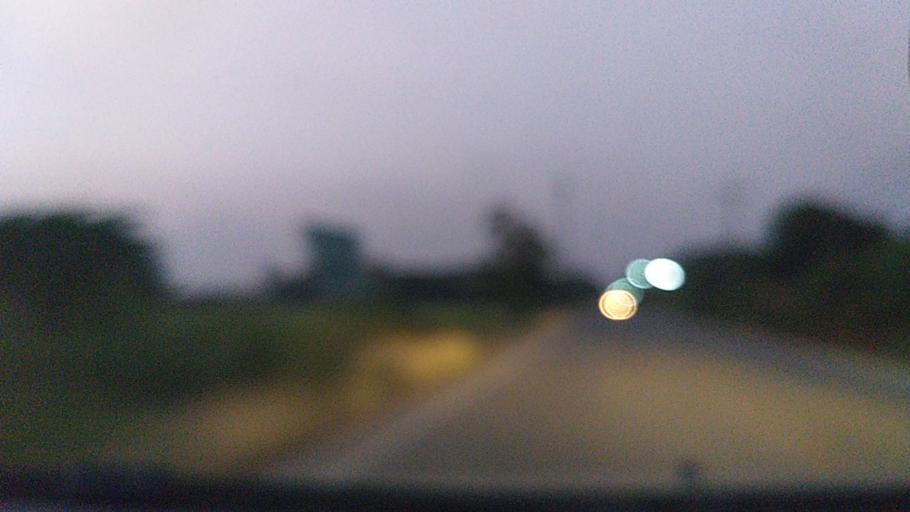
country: TH
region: Sing Buri
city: Sing Buri
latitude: 14.8413
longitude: 100.3934
